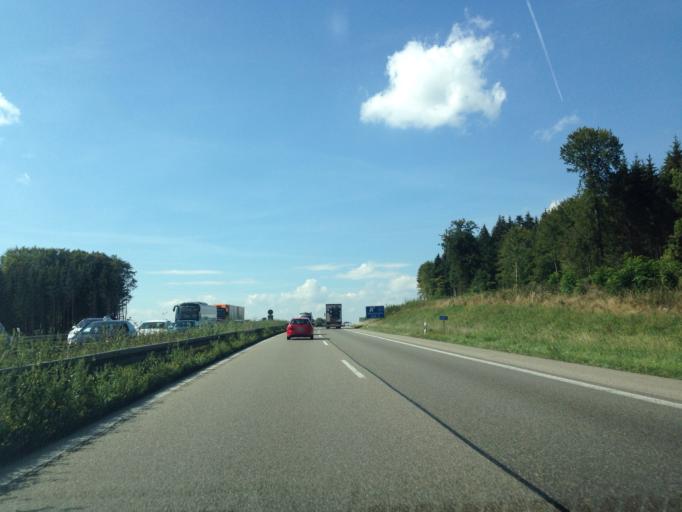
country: DE
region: Baden-Wuerttemberg
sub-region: Tuebingen Region
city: Merklingen
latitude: 48.5181
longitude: 9.7800
